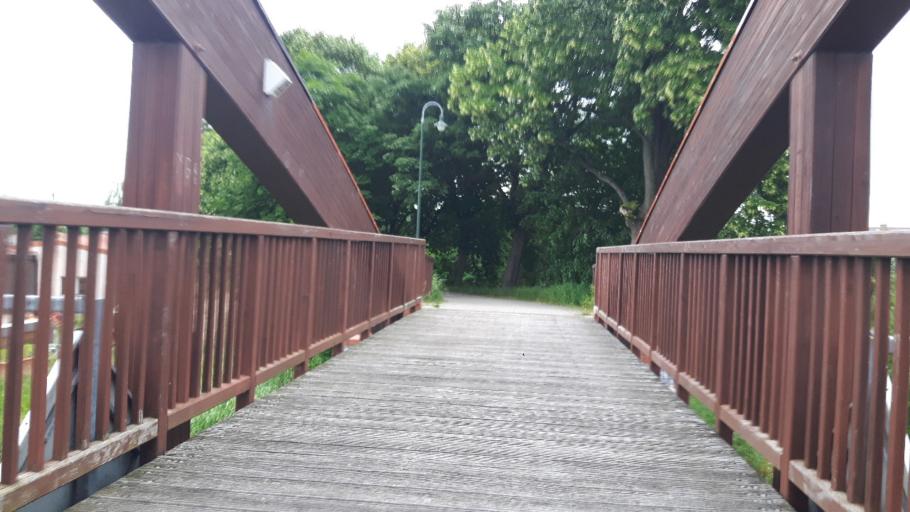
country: DE
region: Brandenburg
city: Schwedt (Oder)
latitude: 53.0470
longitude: 14.2744
